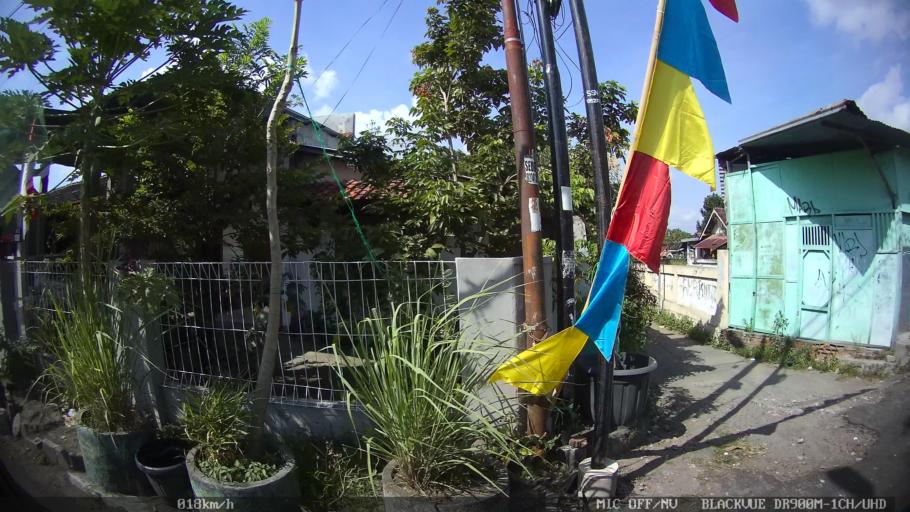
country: ID
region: Daerah Istimewa Yogyakarta
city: Yogyakarta
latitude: -7.8209
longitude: 110.3699
